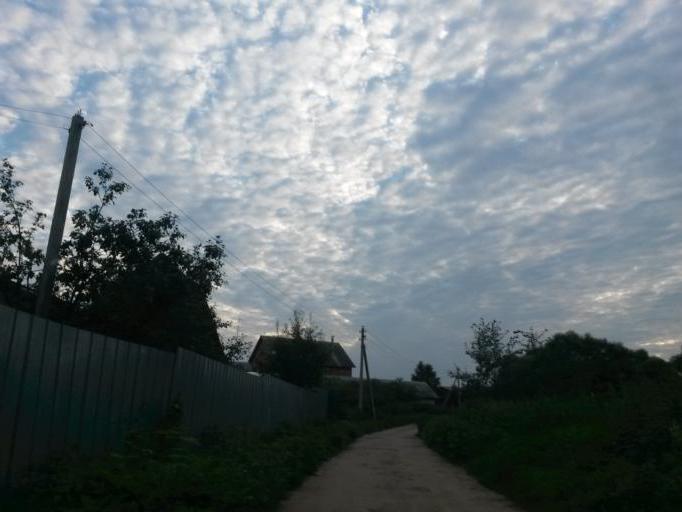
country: RU
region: Moskovskaya
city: Lyubuchany
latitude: 55.2556
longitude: 37.6126
